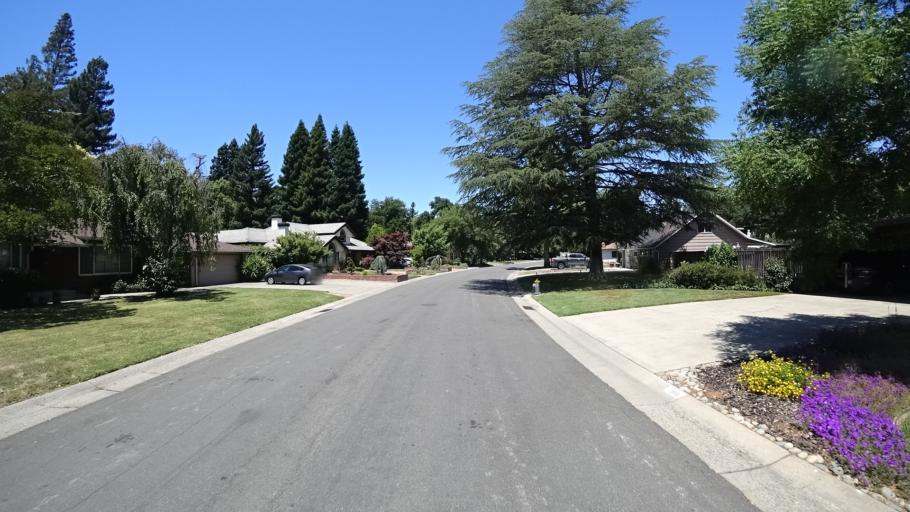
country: US
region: California
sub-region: Yolo County
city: West Sacramento
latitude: 38.5302
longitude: -121.5223
